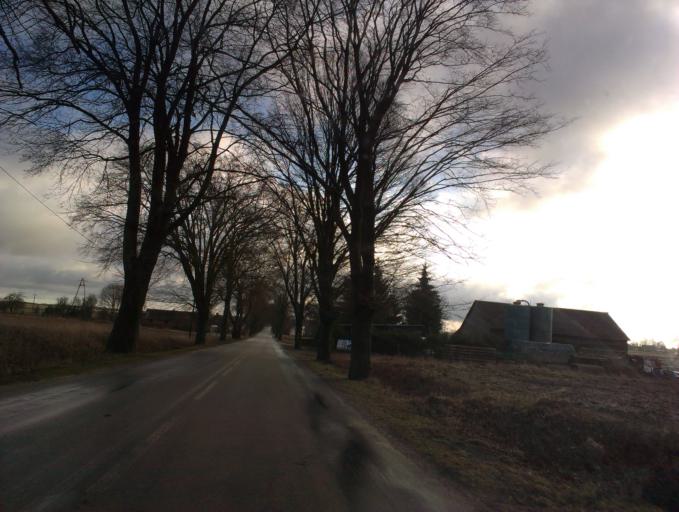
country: PL
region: Pomeranian Voivodeship
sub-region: Powiat czluchowski
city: Czarne
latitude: 53.6870
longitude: 16.9689
